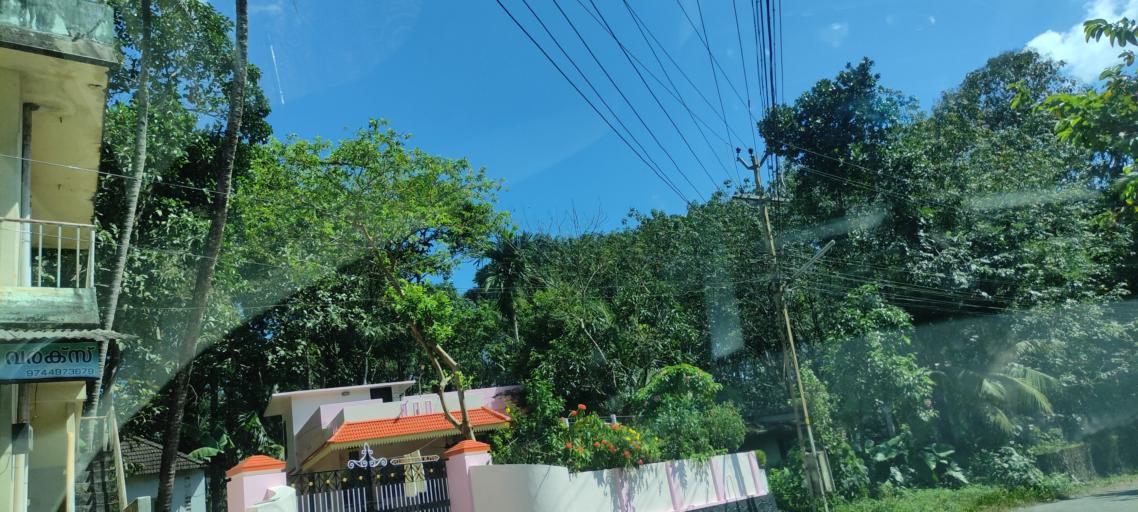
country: IN
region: Kerala
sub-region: Pattanamtitta
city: Adur
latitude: 9.1073
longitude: 76.6874
